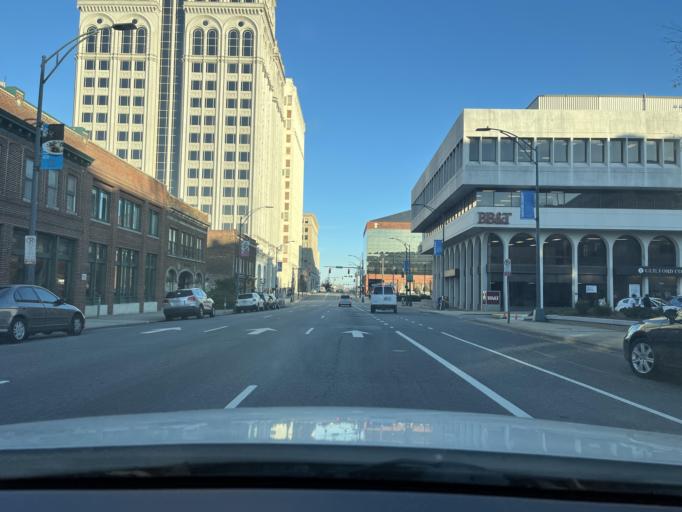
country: US
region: North Carolina
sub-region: Guilford County
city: Greensboro
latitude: 36.0726
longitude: -79.7926
